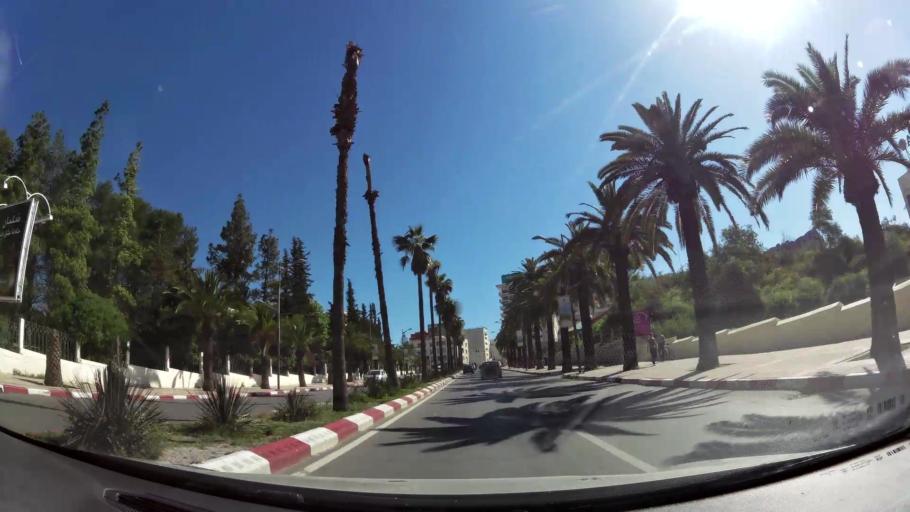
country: MA
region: Meknes-Tafilalet
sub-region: Meknes
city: Meknes
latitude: 33.8969
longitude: -5.5542
